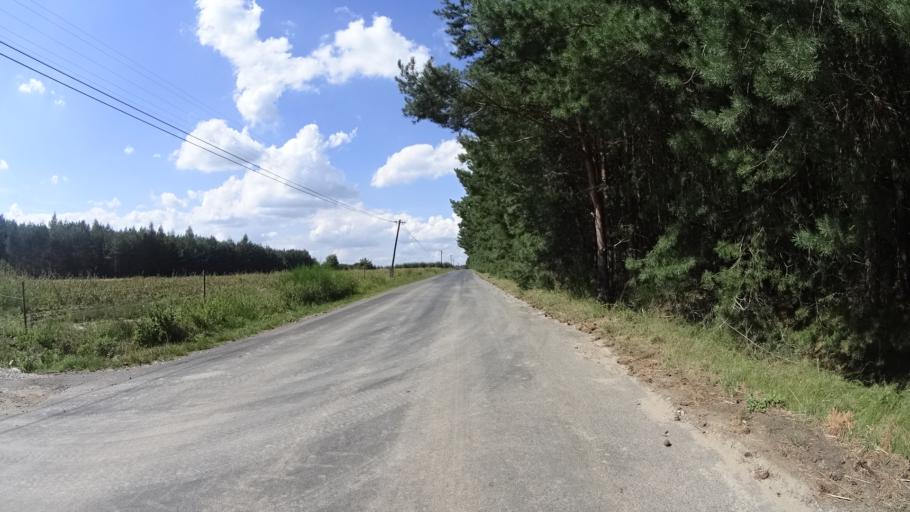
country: PL
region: Masovian Voivodeship
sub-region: Powiat grojecki
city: Mogielnica
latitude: 51.6853
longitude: 20.7564
